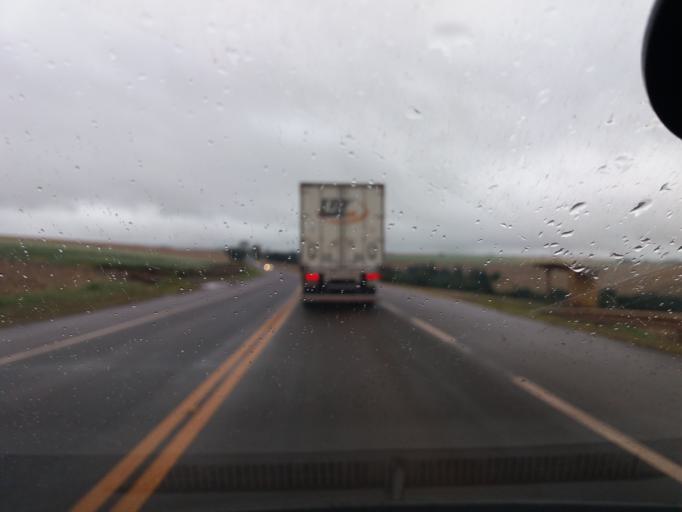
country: BR
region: Parana
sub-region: Campo Mourao
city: Campo Mourao
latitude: -24.3312
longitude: -52.6576
